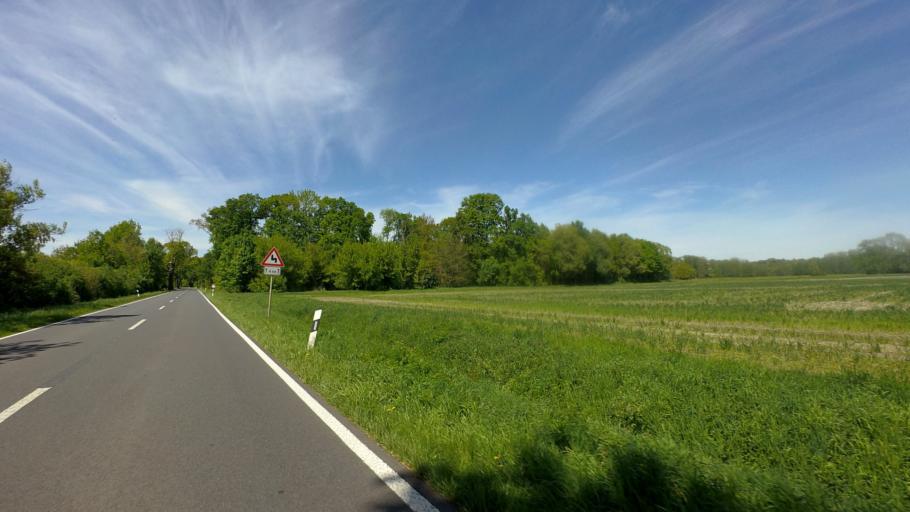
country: DE
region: Brandenburg
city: Baruth
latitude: 52.0800
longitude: 13.4520
